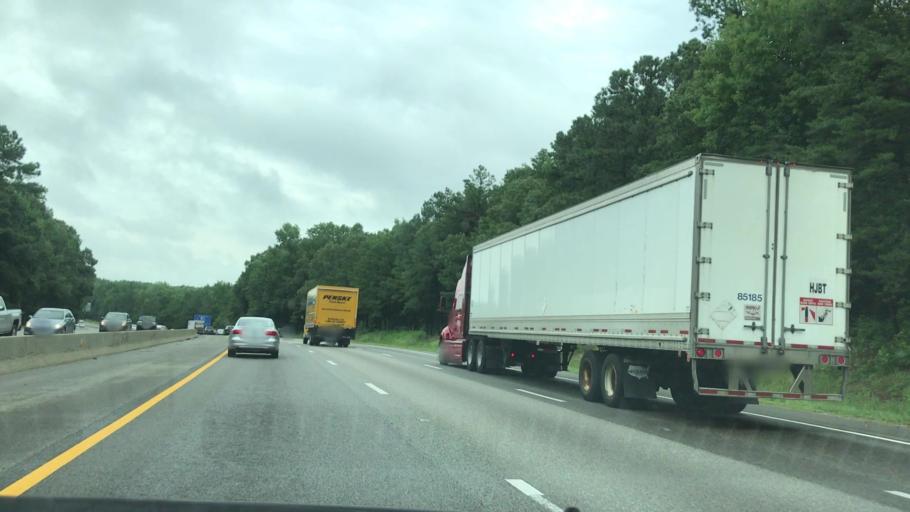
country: US
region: Virginia
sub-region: Chesterfield County
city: Chester
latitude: 37.3257
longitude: -77.3997
